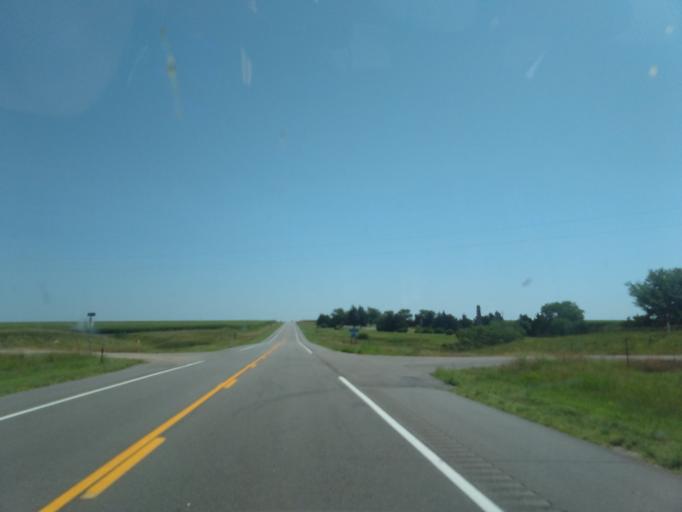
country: US
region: Nebraska
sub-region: Hitchcock County
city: Trenton
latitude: 40.2061
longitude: -100.9672
